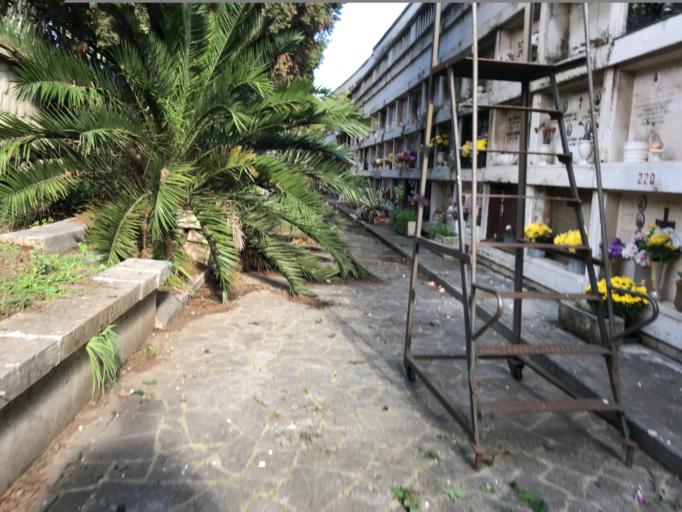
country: IT
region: Latium
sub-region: Citta metropolitana di Roma Capitale
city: Rome
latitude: 41.9051
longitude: 12.5323
